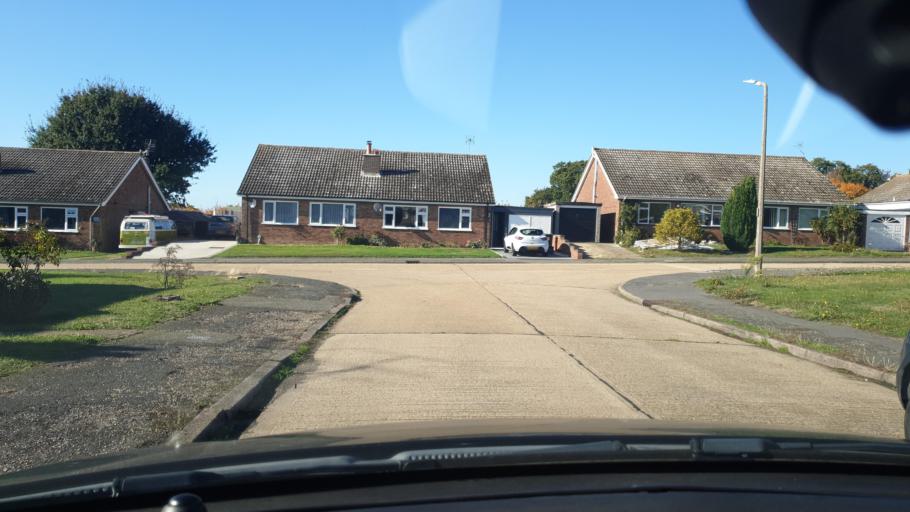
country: GB
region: England
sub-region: Essex
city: Little Clacton
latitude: 51.8984
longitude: 1.1815
